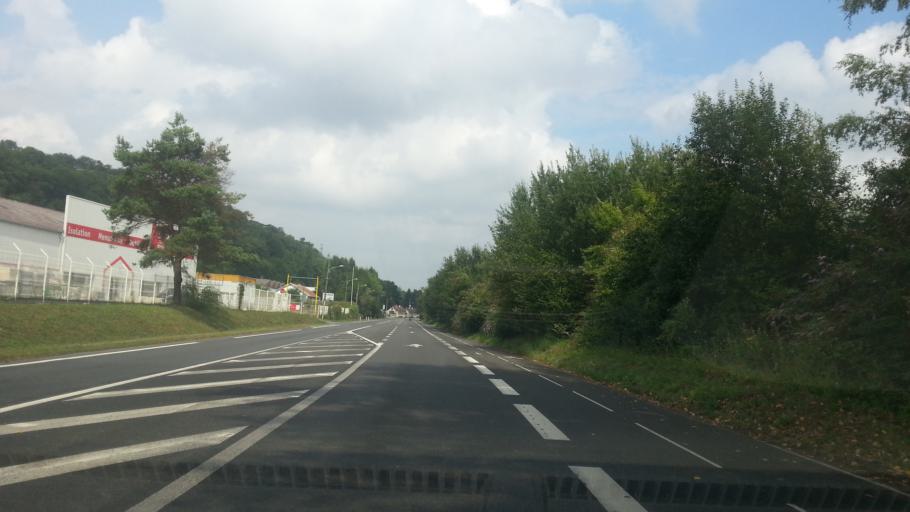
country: FR
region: Picardie
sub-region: Departement de l'Oise
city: Thiverny
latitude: 49.2336
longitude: 2.4357
